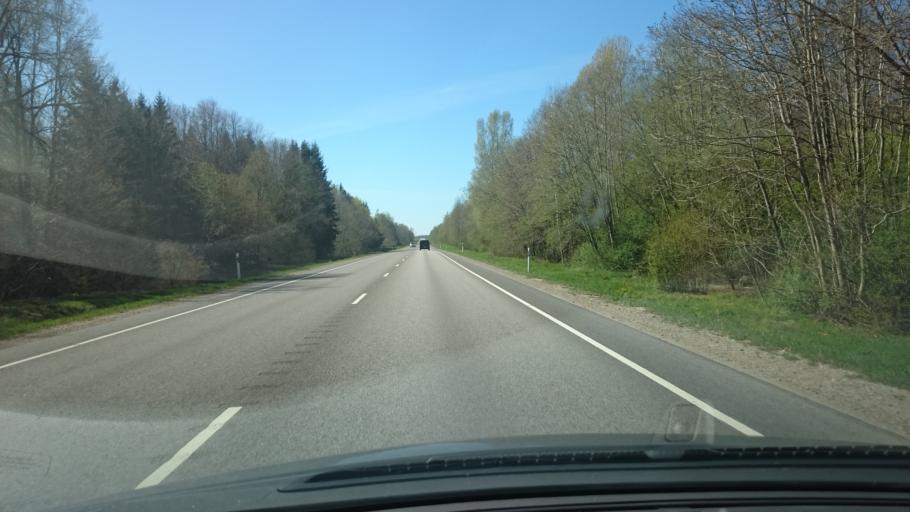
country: EE
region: Ida-Virumaa
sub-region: Sillamaee linn
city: Sillamae
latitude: 59.3813
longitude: 27.8538
